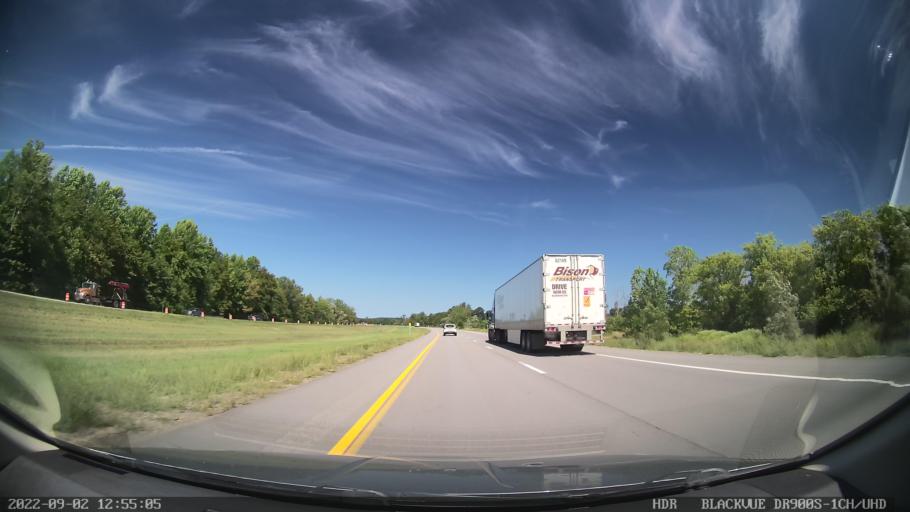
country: US
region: New York
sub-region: Livingston County
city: Avon
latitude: 42.9346
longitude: -77.6909
